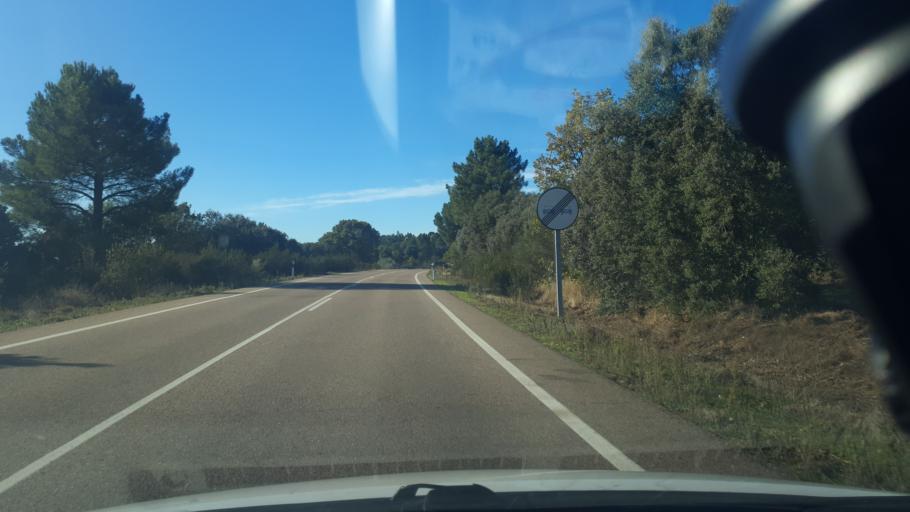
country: ES
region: Castille and Leon
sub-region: Provincia de Avila
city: Arenas de San Pedro
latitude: 40.1717
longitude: -5.0967
